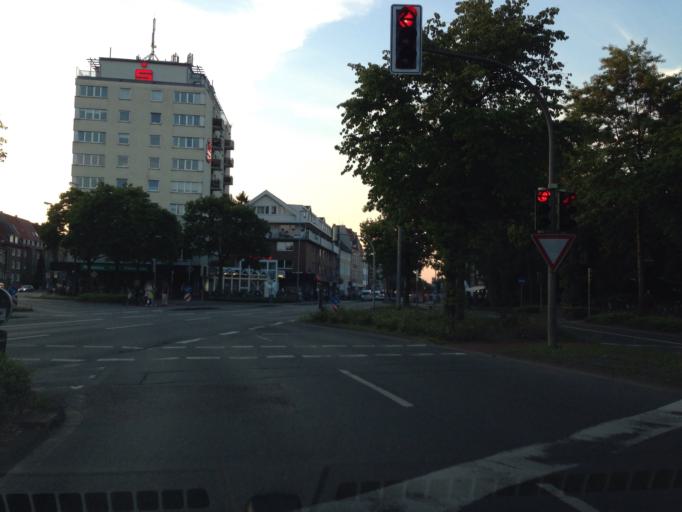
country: DE
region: North Rhine-Westphalia
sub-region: Regierungsbezirk Munster
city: Muenster
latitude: 51.9450
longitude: 7.6232
